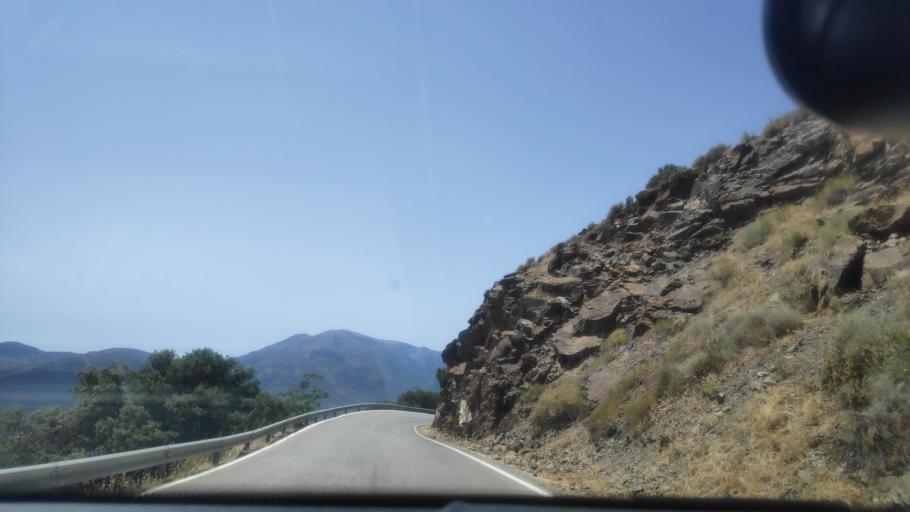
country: ES
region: Andalusia
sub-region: Provincia de Granada
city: Pampaneira
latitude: 36.9245
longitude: -3.3509
